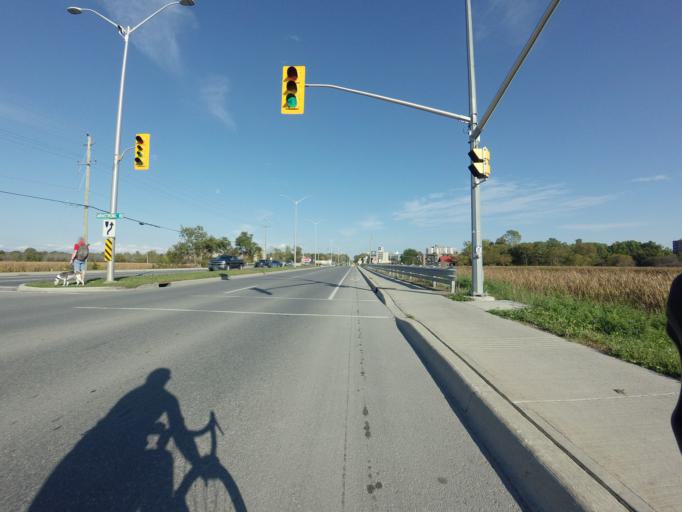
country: CA
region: Ontario
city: Kingston
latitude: 44.2381
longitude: -76.5420
